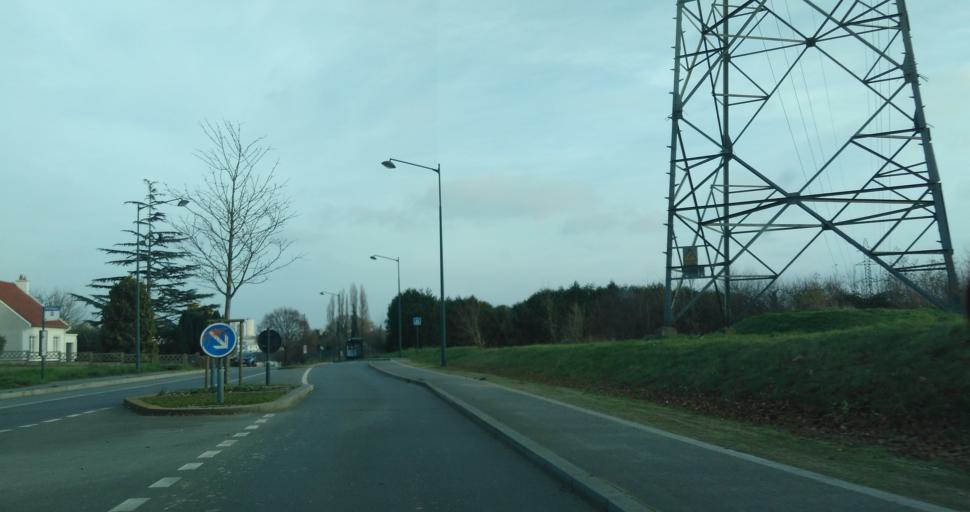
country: FR
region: Brittany
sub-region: Departement d'Ille-et-Vilaine
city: Vezin-le-Coquet
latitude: 48.1166
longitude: -1.7245
